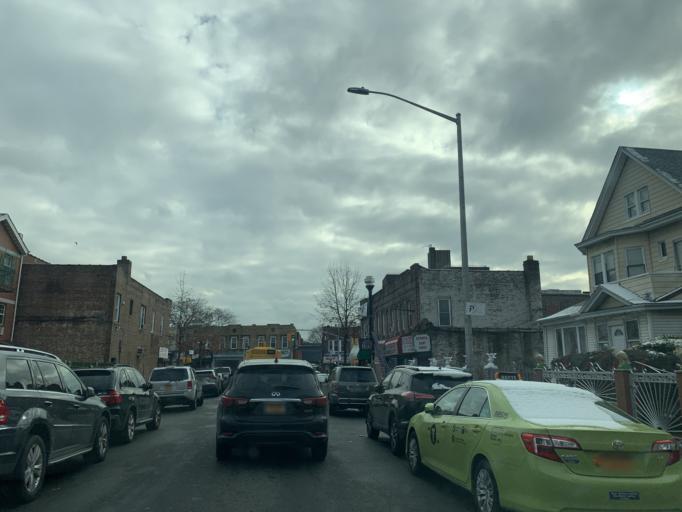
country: US
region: New York
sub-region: Queens County
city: Jamaica
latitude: 40.7081
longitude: -73.7890
